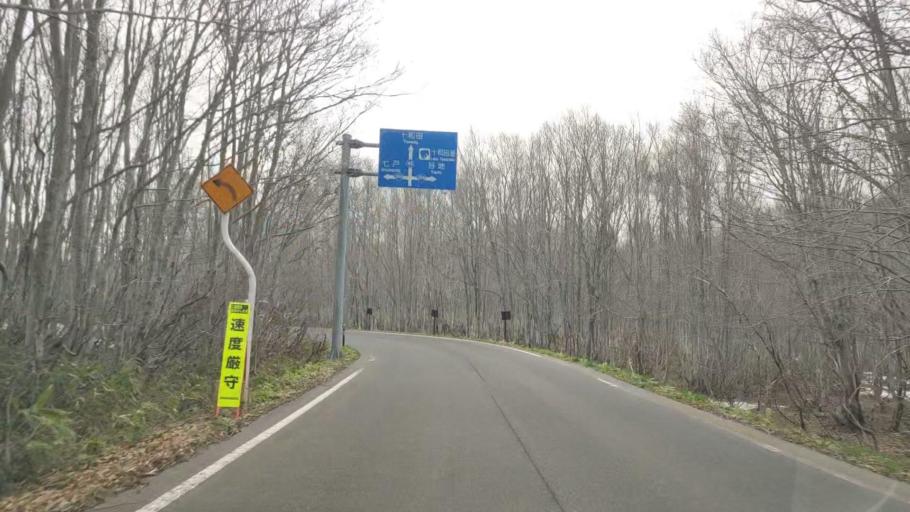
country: JP
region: Aomori
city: Aomori Shi
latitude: 40.6644
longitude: 140.9574
